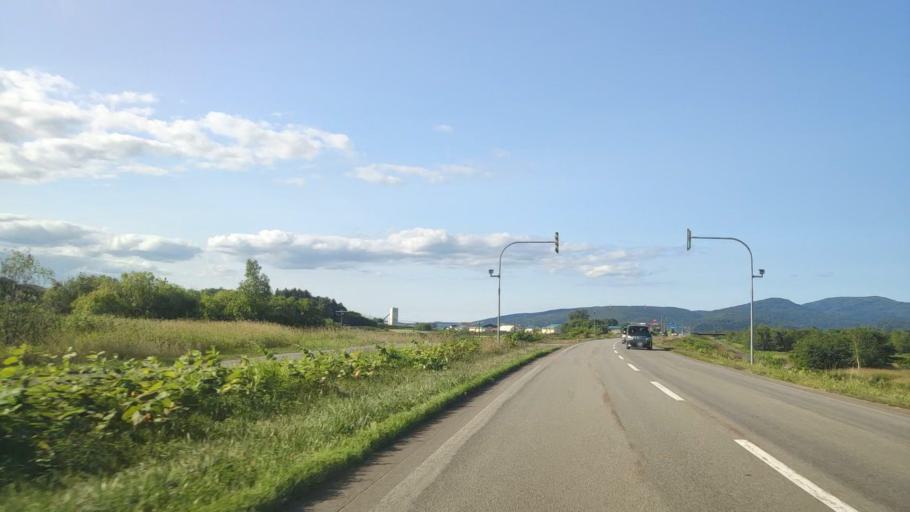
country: JP
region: Hokkaido
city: Nayoro
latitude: 44.8123
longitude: 142.0659
